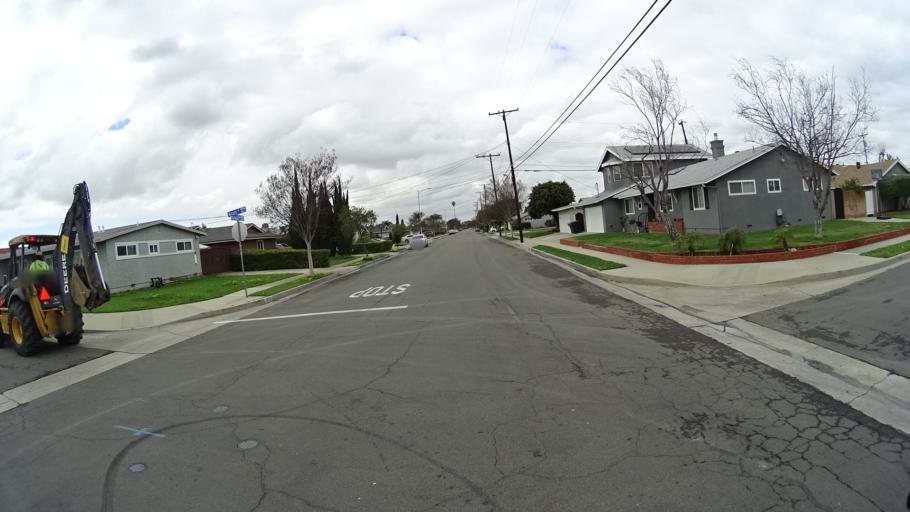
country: US
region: California
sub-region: Orange County
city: Anaheim
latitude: 33.8296
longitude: -117.9519
